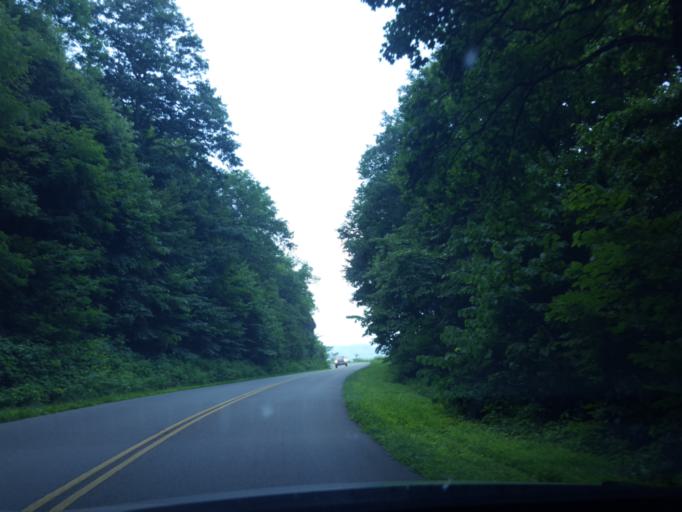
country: US
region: Virginia
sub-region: Nelson County
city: Nellysford
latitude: 37.9144
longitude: -78.9708
